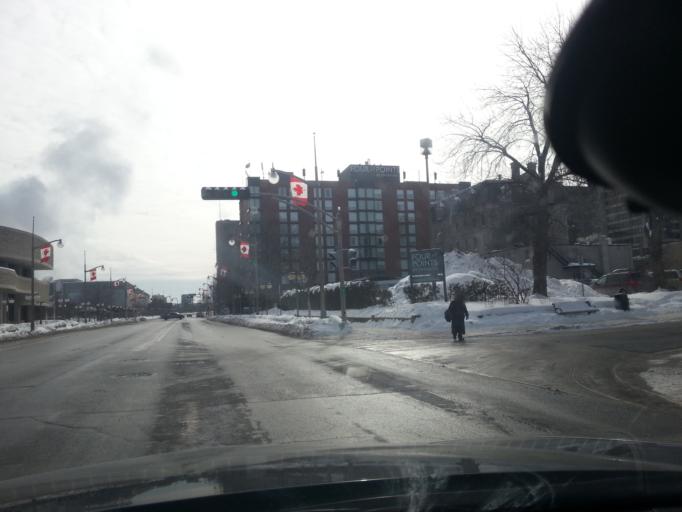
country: CA
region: Ontario
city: Ottawa
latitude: 45.4298
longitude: -75.7102
